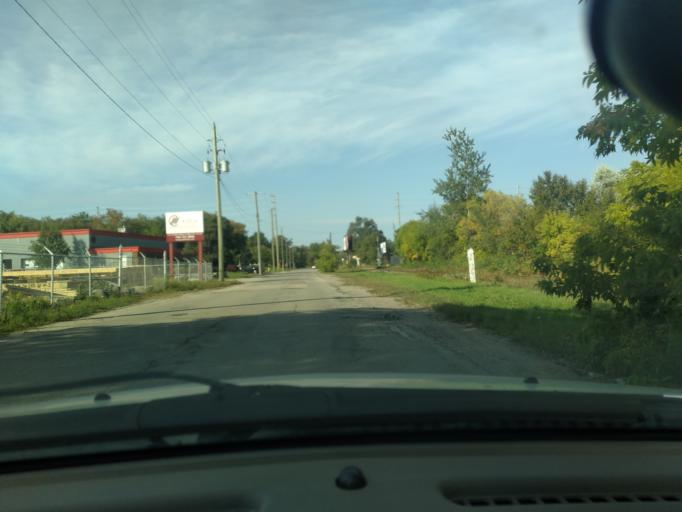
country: CA
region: Ontario
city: Barrie
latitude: 44.3726
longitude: -79.6952
